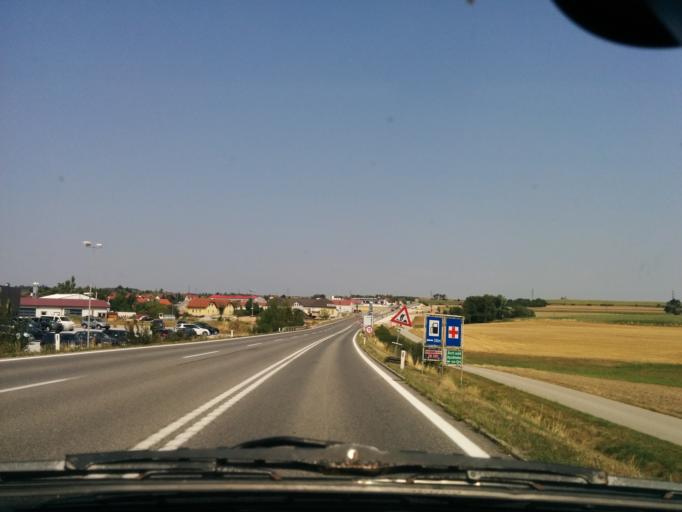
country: AT
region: Lower Austria
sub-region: Politischer Bezirk Krems
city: Gfohl
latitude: 48.5090
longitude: 15.5130
